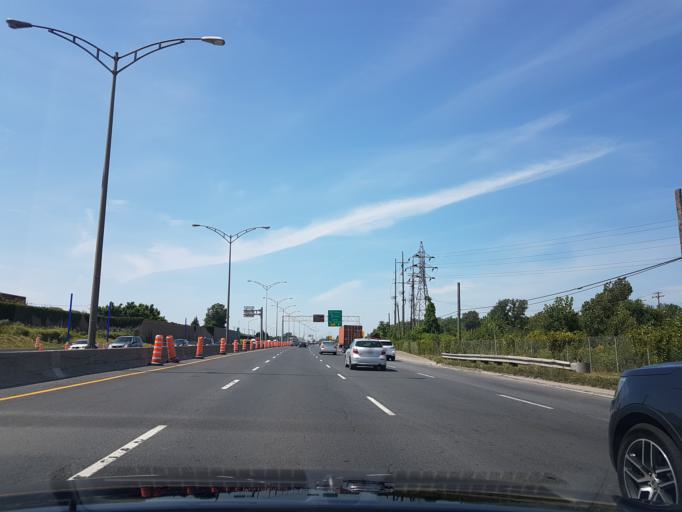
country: CA
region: Quebec
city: Cote-Saint-Luc
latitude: 45.4475
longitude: -73.6835
